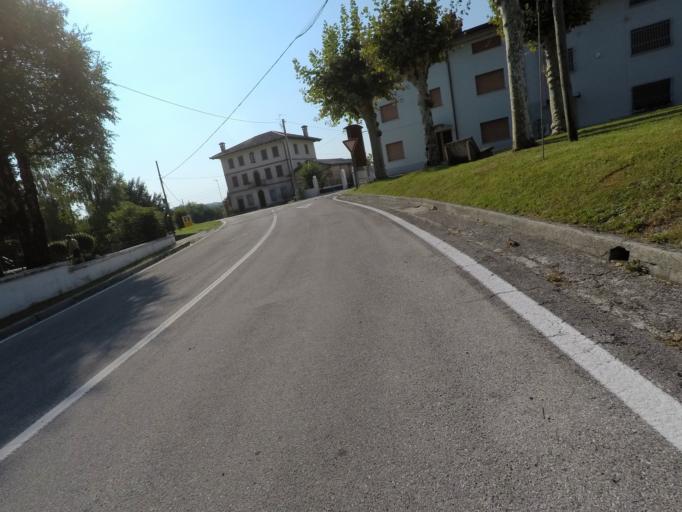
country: IT
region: Friuli Venezia Giulia
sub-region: Provincia di Pordenone
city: Pinzano al Tagliamento
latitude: 46.1844
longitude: 12.9489
